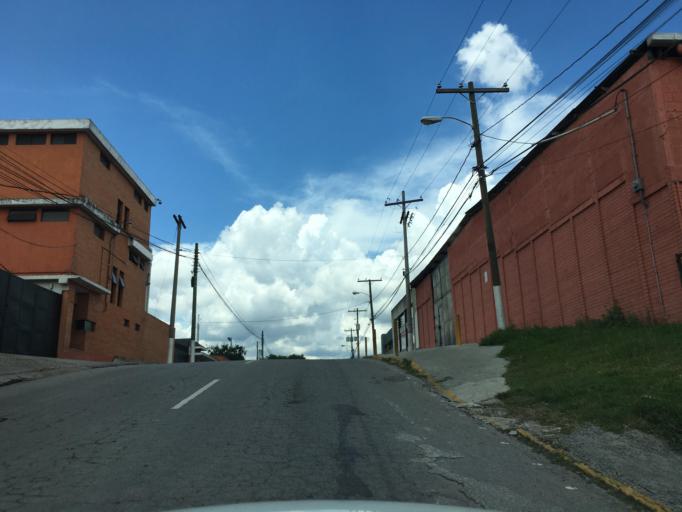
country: GT
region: Guatemala
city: Santa Catarina Pinula
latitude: 14.5899
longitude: -90.5487
